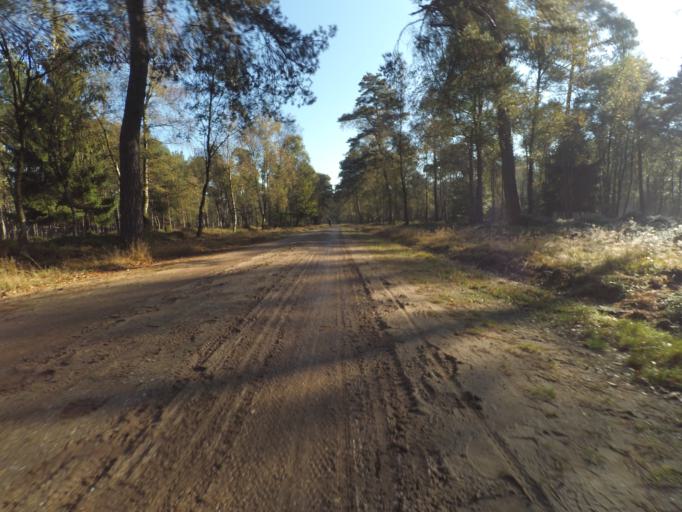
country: NL
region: Gelderland
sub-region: Gemeente Epe
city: Vaassen
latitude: 52.2516
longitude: 5.9139
